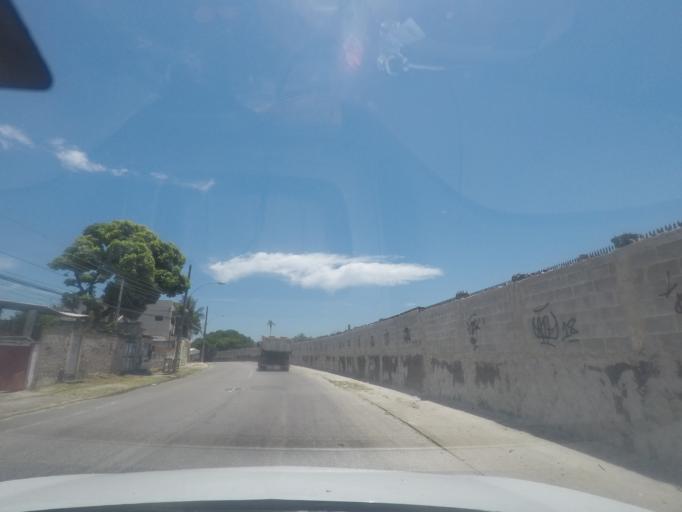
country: BR
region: Rio de Janeiro
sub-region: Itaguai
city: Itaguai
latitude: -22.9210
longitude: -43.6915
